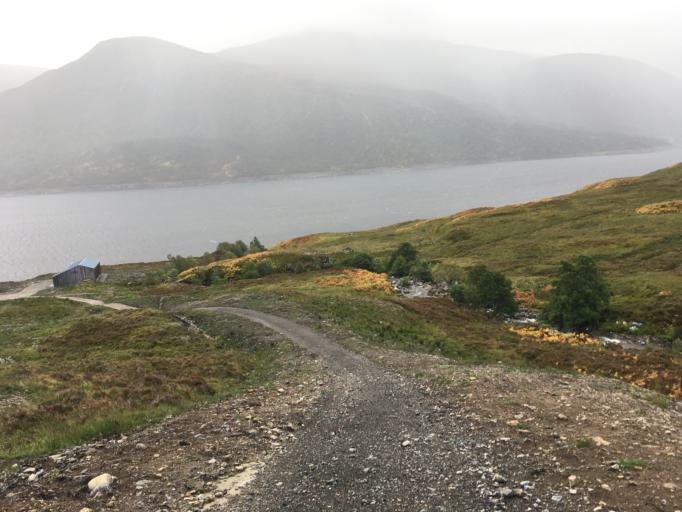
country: GB
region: Scotland
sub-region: Highland
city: Spean Bridge
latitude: 57.3433
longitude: -4.9823
